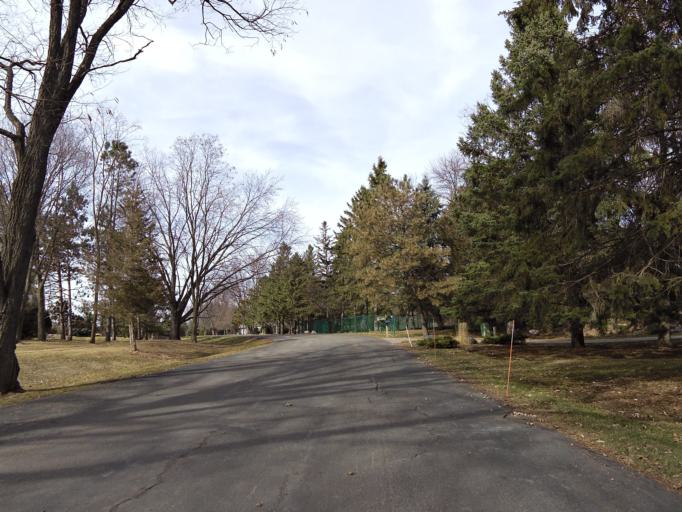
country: US
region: Minnesota
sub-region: Washington County
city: Lakeland
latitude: 44.9436
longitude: -92.7831
